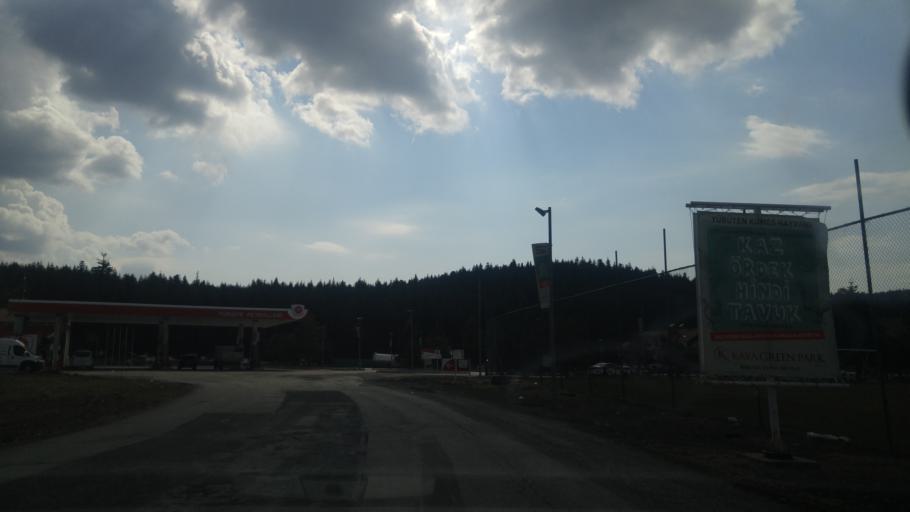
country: TR
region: Ankara
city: Pecenek
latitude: 40.6096
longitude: 32.2525
